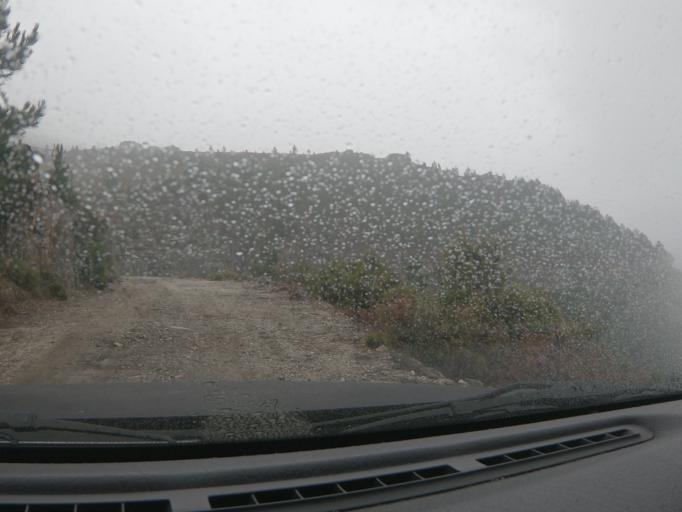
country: PT
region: Vila Real
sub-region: Vila Real
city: Vila Real
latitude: 41.3723
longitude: -7.7460
